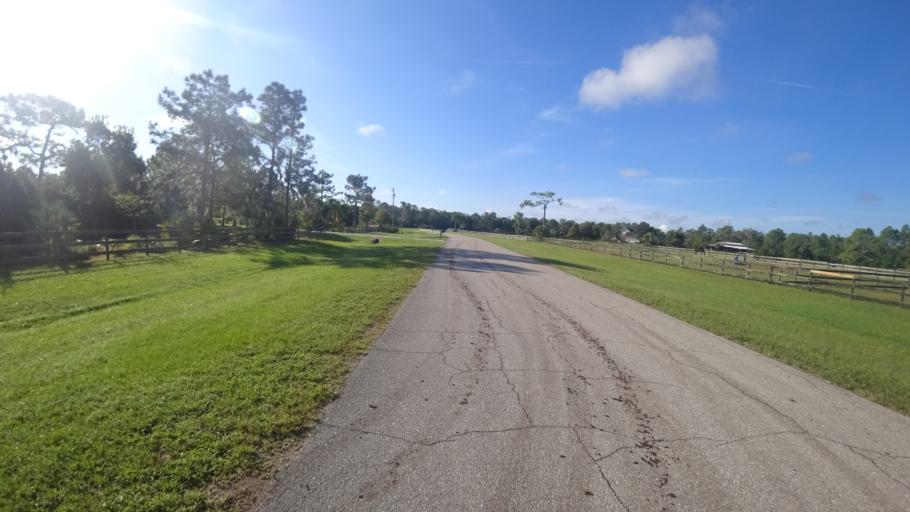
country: US
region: Florida
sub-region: Sarasota County
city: The Meadows
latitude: 27.4196
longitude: -82.3437
